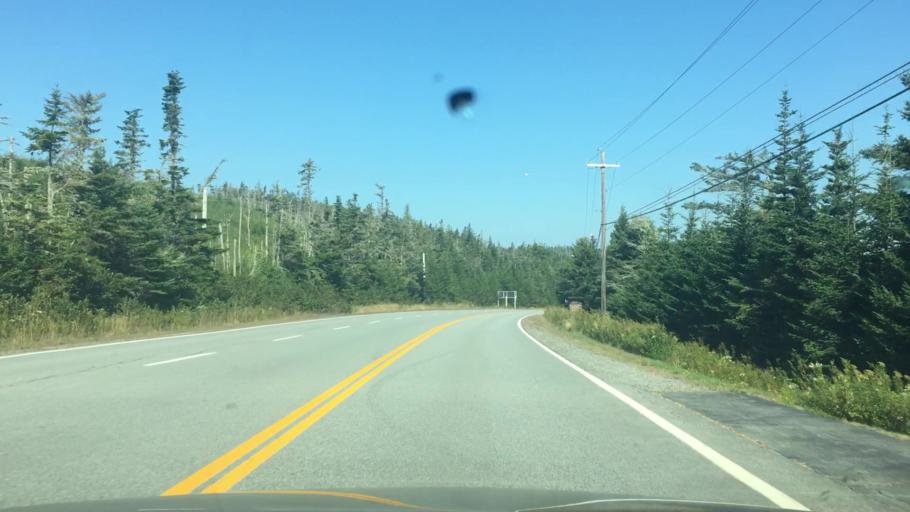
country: CA
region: Nova Scotia
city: New Glasgow
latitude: 44.8176
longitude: -62.6329
